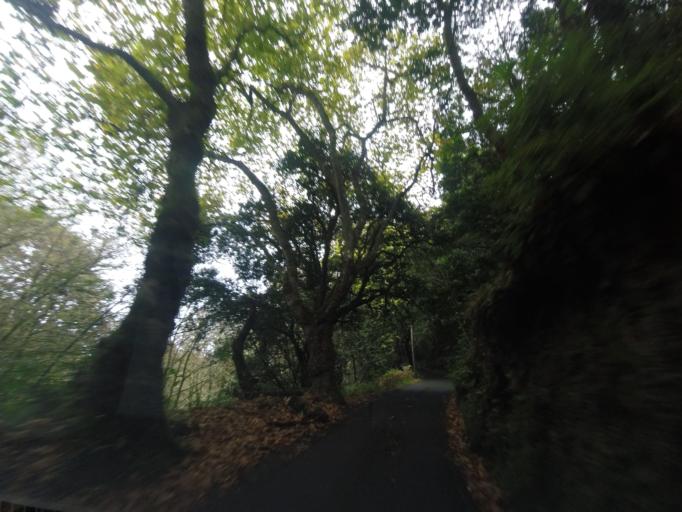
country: PT
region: Madeira
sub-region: Santana
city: Santana
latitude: 32.7845
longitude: -16.9016
